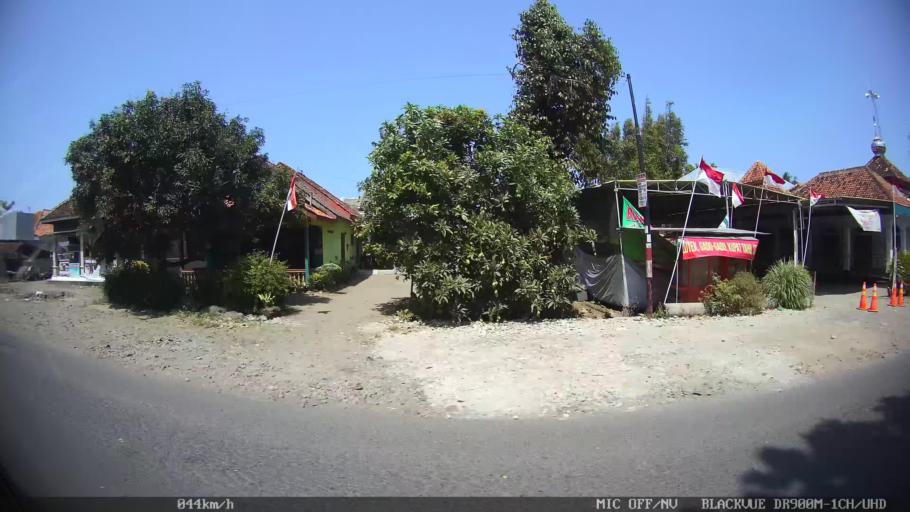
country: ID
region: Daerah Istimewa Yogyakarta
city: Srandakan
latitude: -7.9078
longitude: 110.0825
